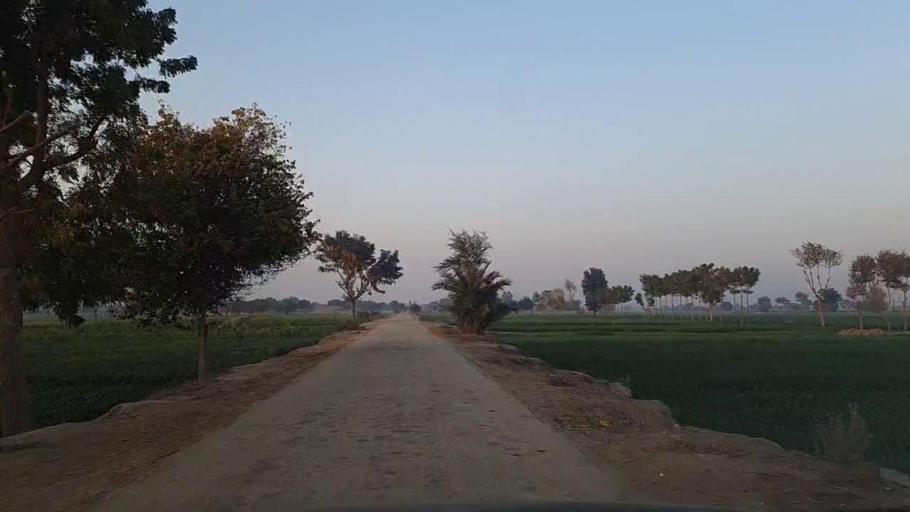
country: PK
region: Sindh
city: Jam Sahib
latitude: 26.4654
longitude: 68.5420
